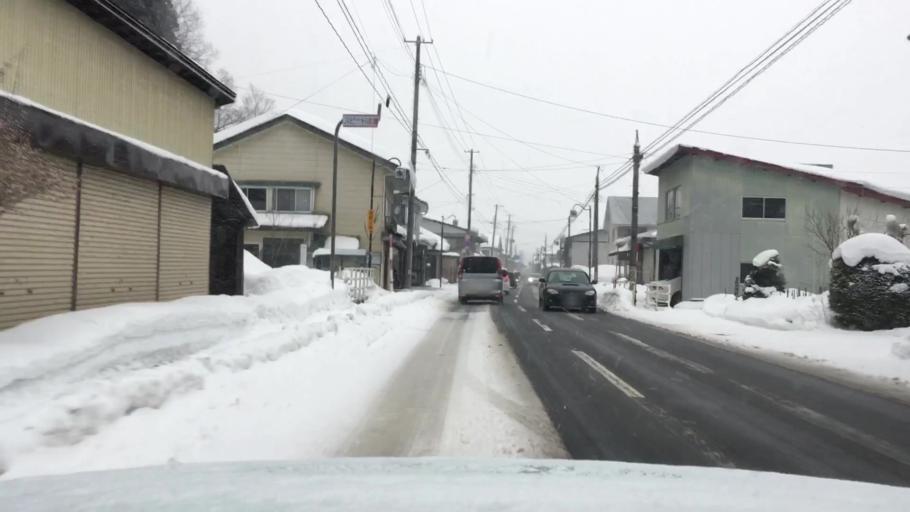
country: JP
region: Iwate
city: Ichinohe
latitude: 40.0951
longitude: 141.0472
